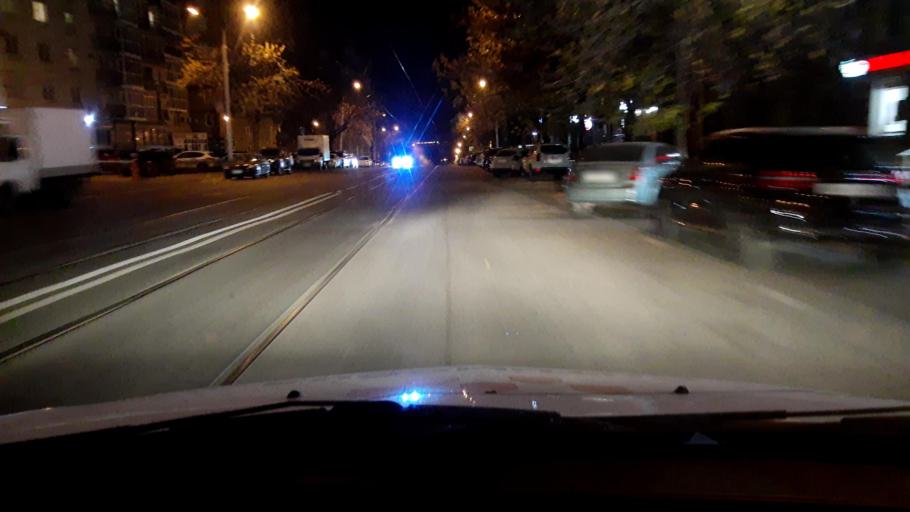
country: RU
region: Bashkortostan
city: Ufa
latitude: 54.7463
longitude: 55.9590
